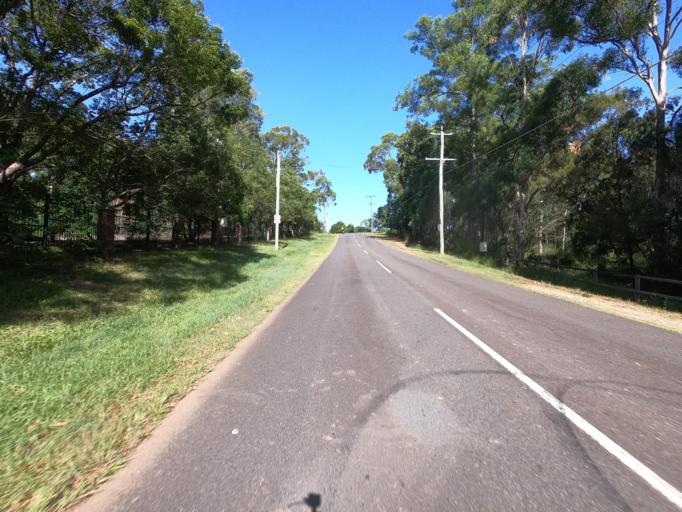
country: AU
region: Queensland
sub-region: Brisbane
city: Burbank
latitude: -27.5593
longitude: 153.1353
